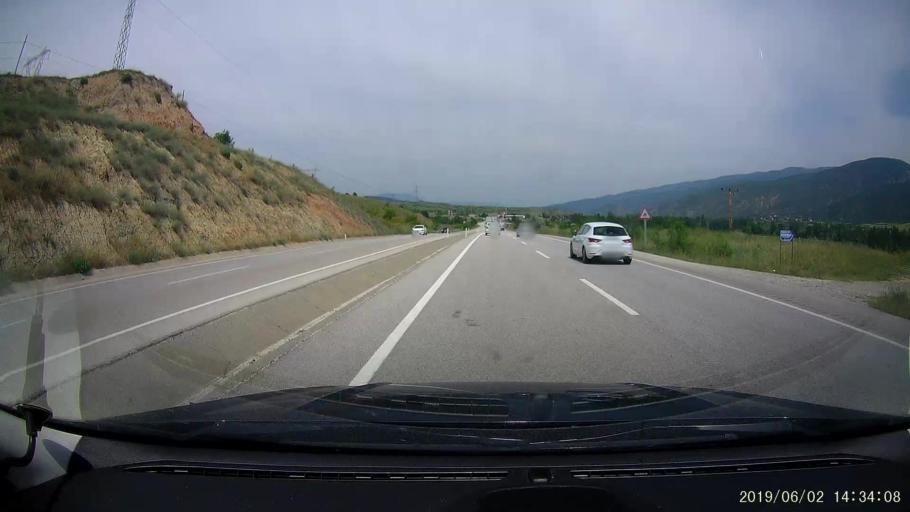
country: TR
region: Kastamonu
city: Tosya
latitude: 41.0366
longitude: 34.1862
